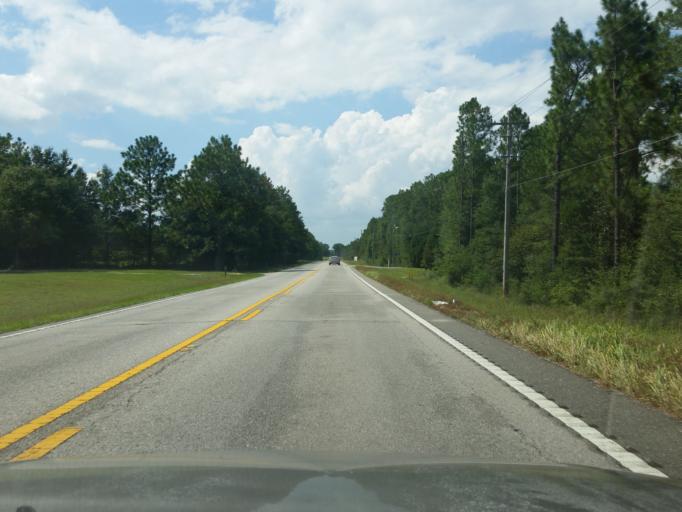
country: US
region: Alabama
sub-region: Baldwin County
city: Elberta
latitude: 30.5166
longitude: -87.4779
